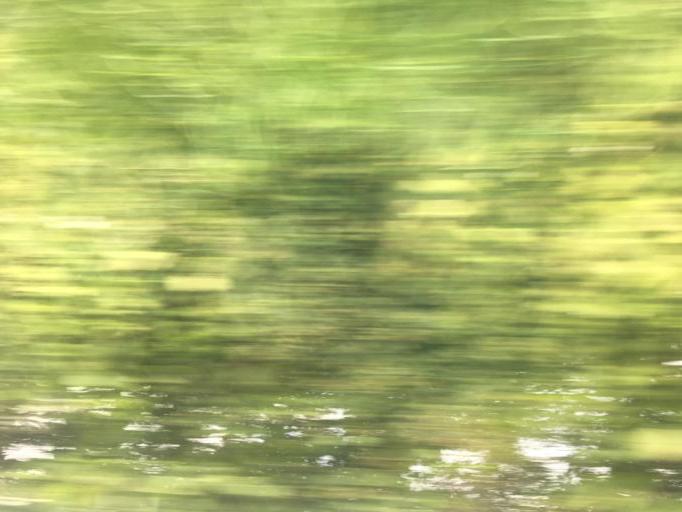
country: GB
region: Wales
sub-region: County of Ceredigion
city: Lampeter
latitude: 52.1277
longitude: -4.0754
